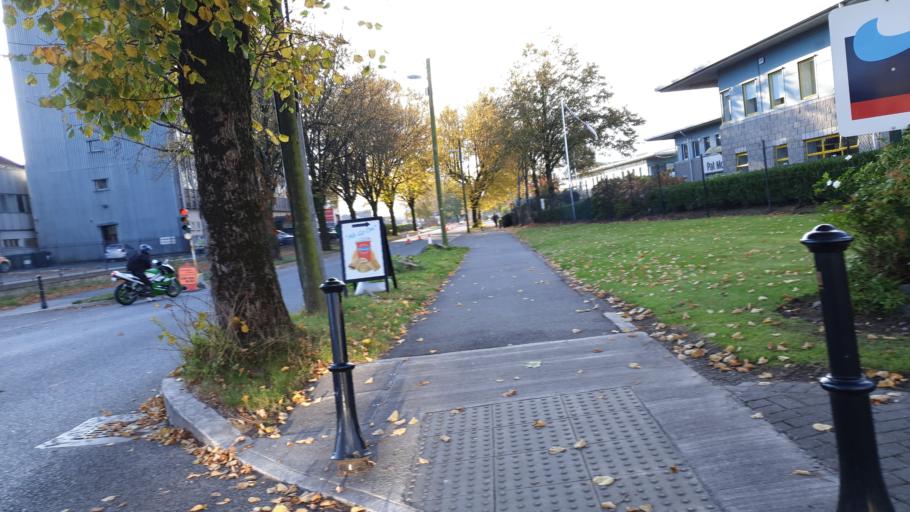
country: IE
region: Munster
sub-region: County Cork
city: Cork
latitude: 51.8981
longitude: -8.4483
